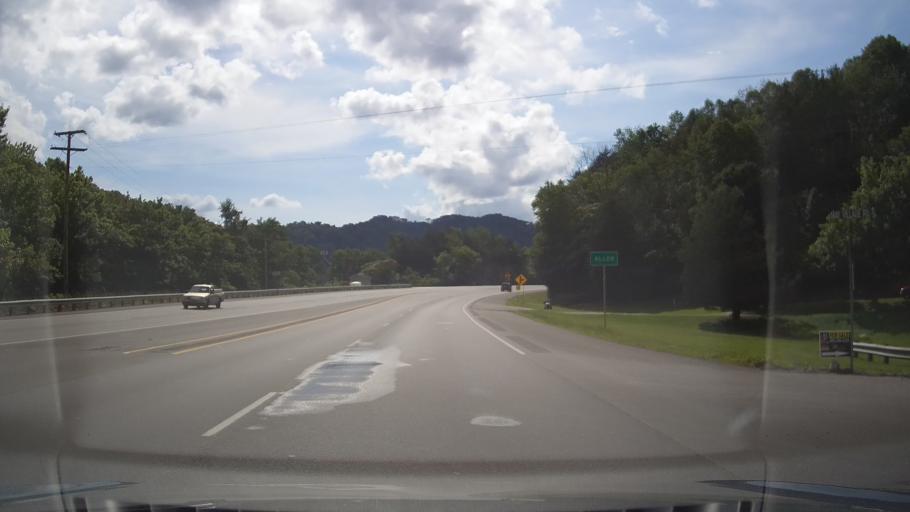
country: US
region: Kentucky
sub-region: Floyd County
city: Prestonsburg
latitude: 37.6133
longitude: -82.7155
